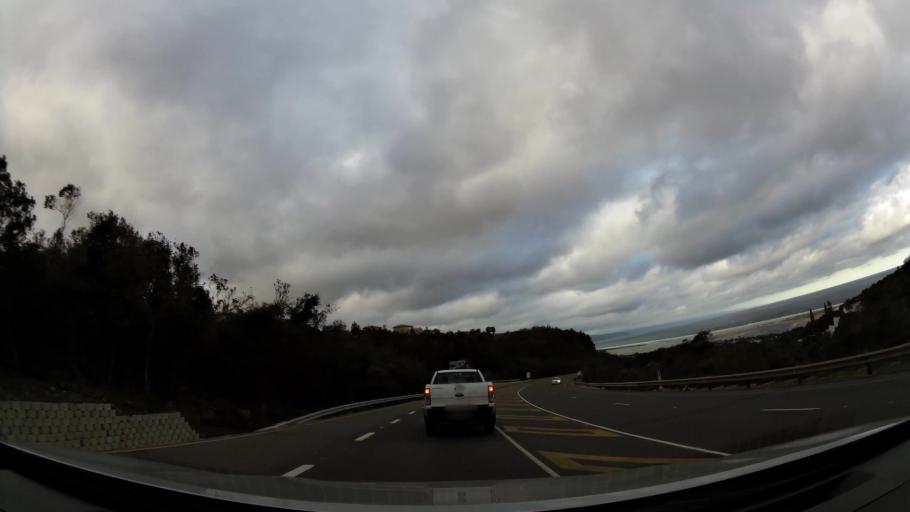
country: ZA
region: Western Cape
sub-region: Eden District Municipality
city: Plettenberg Bay
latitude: -34.0450
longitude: 23.3626
